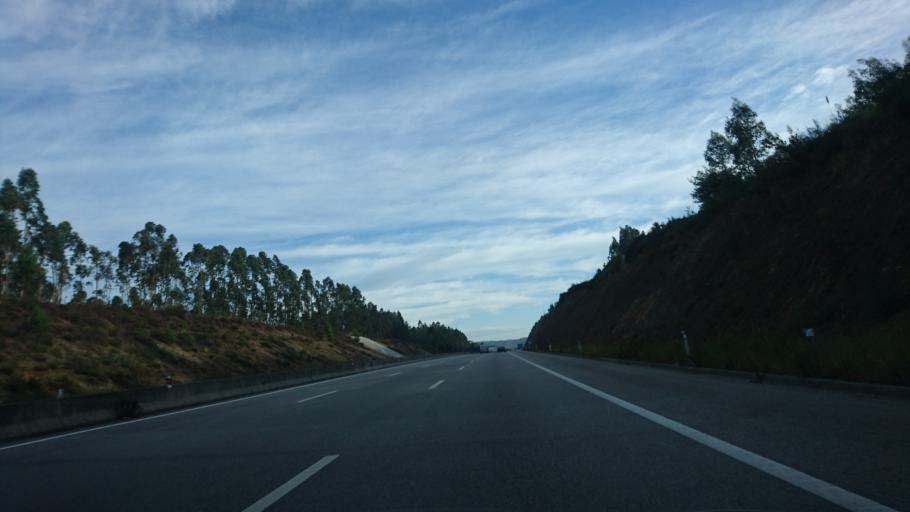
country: PT
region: Porto
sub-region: Vila Nova de Gaia
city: Sandim
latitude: 41.0491
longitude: -8.4761
